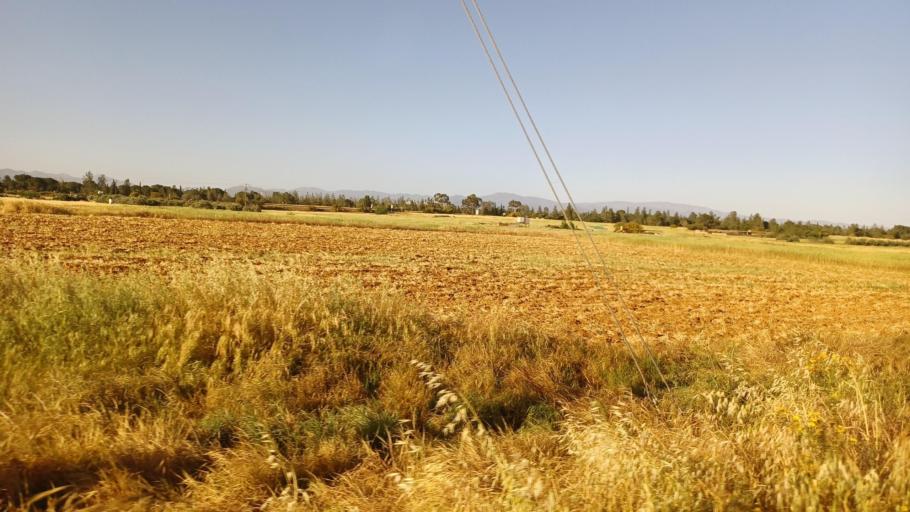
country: CY
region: Lefkosia
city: Kokkinotrimithia
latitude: 35.1499
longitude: 33.1787
